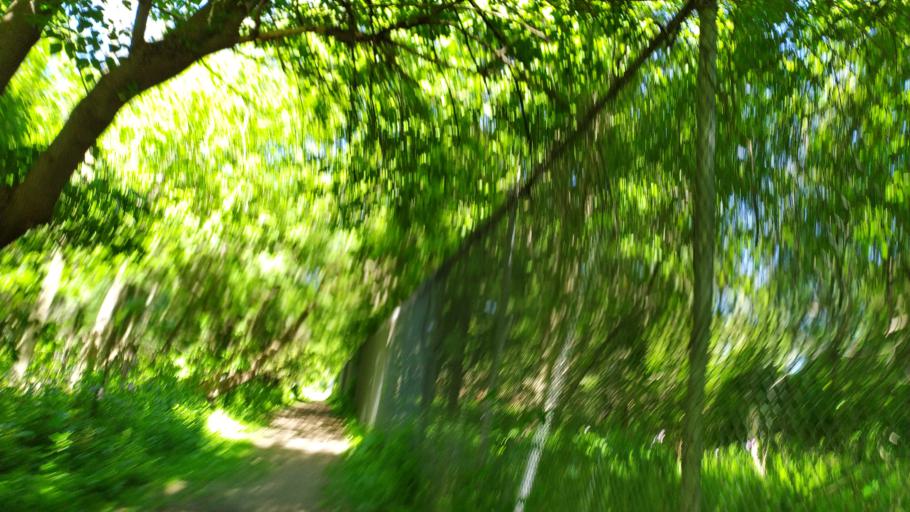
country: CA
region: Ontario
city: Stratford
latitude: 43.3688
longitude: -81.0072
